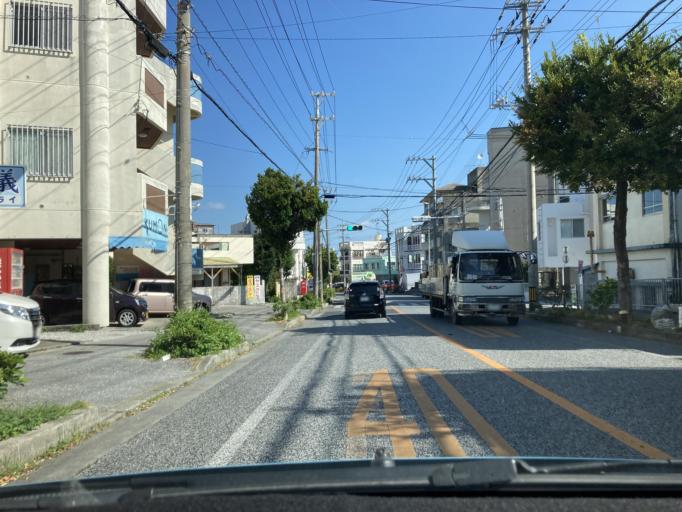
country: JP
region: Okinawa
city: Ginowan
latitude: 26.2619
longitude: 127.7234
